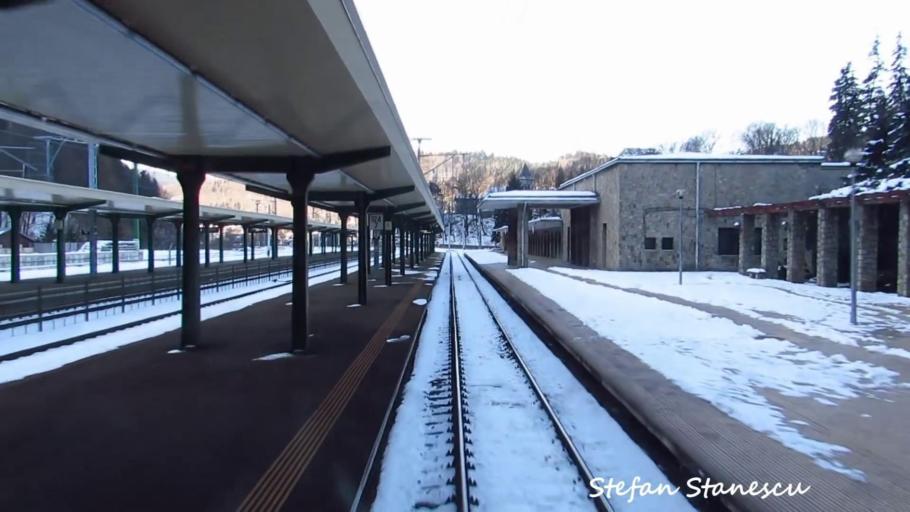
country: RO
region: Prahova
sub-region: Oras Sinaia
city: Sinaia
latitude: 45.3572
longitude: 25.5561
